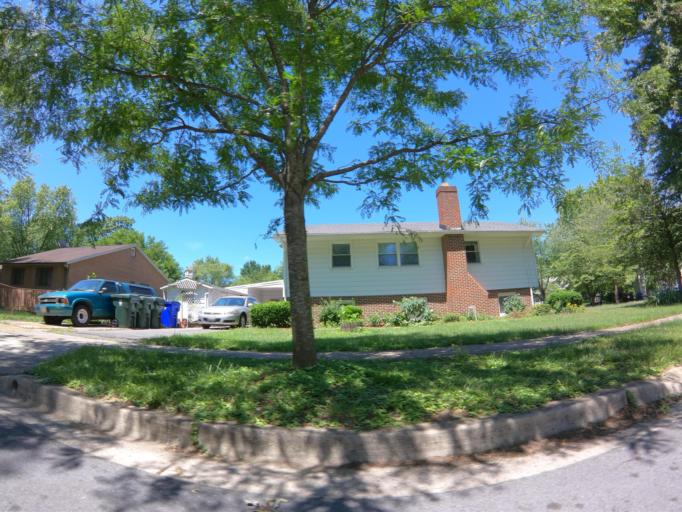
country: US
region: Maryland
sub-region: Prince George's County
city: College Park
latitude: 38.9900
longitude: -76.9258
